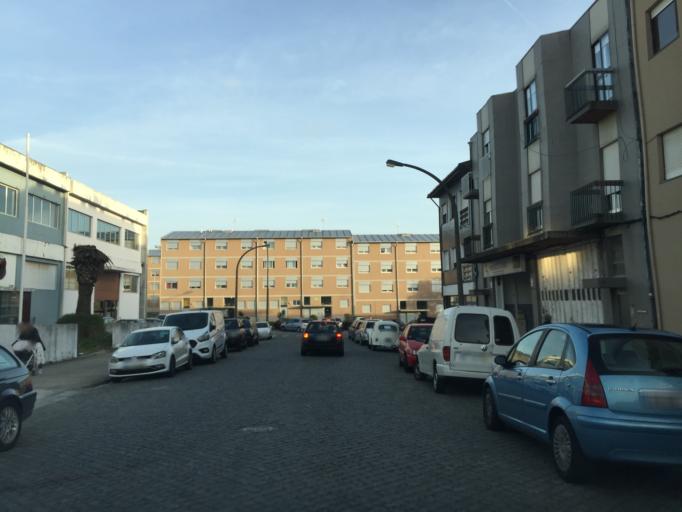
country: PT
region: Porto
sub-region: Matosinhos
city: Senhora da Hora
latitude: 41.1704
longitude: -8.6494
